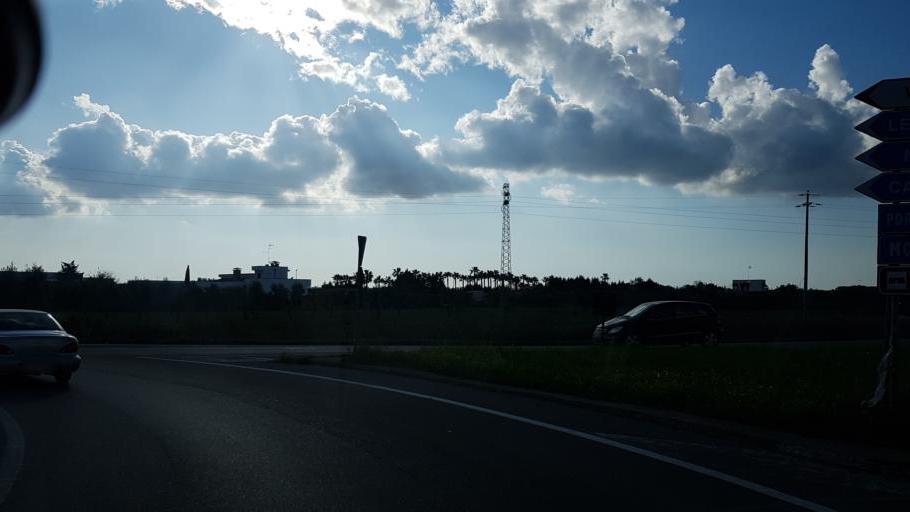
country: IT
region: Apulia
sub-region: Provincia di Lecce
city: Veglie
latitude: 40.3494
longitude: 17.9685
